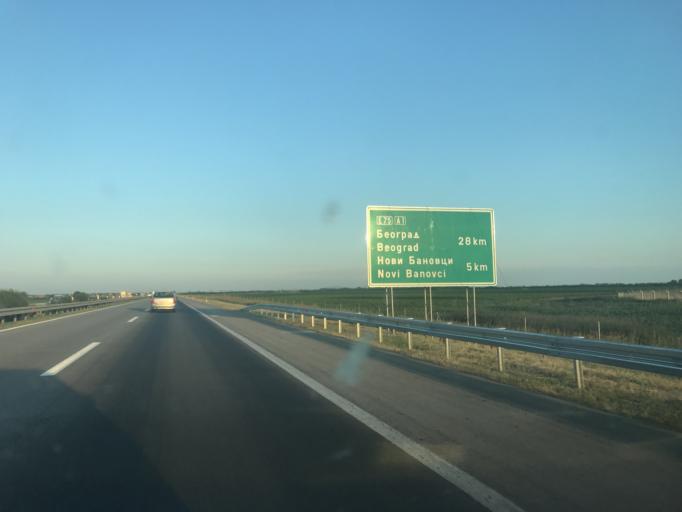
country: RS
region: Autonomna Pokrajina Vojvodina
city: Nova Pazova
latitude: 44.9649
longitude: 20.2427
